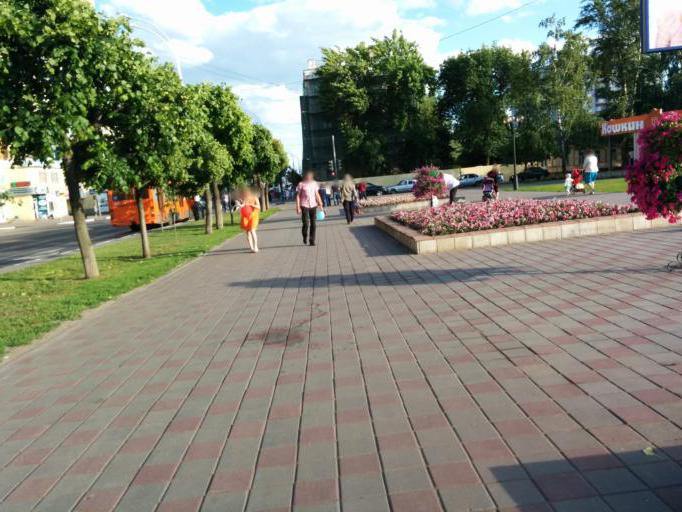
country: RU
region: Tambov
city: Tambov
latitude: 52.7329
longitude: 41.4532
